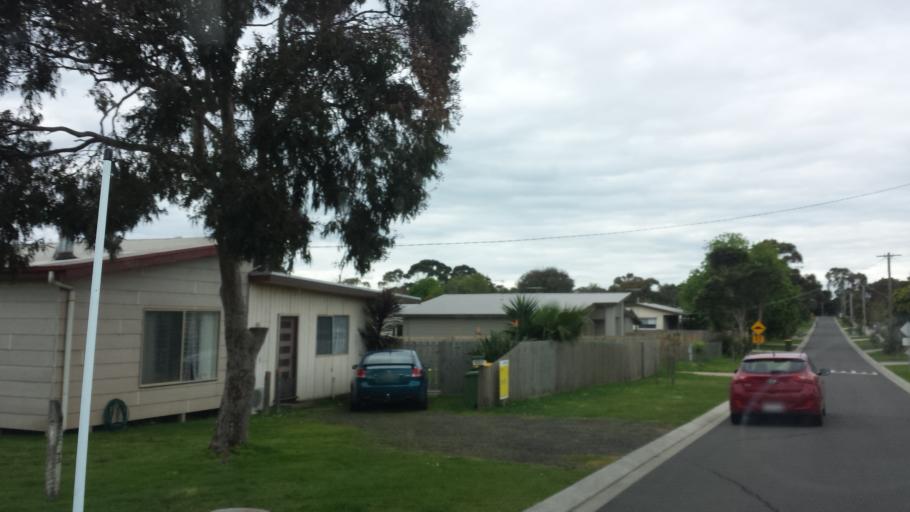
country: AU
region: Victoria
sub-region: Bass Coast
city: Cowes
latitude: -38.4594
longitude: 145.2107
